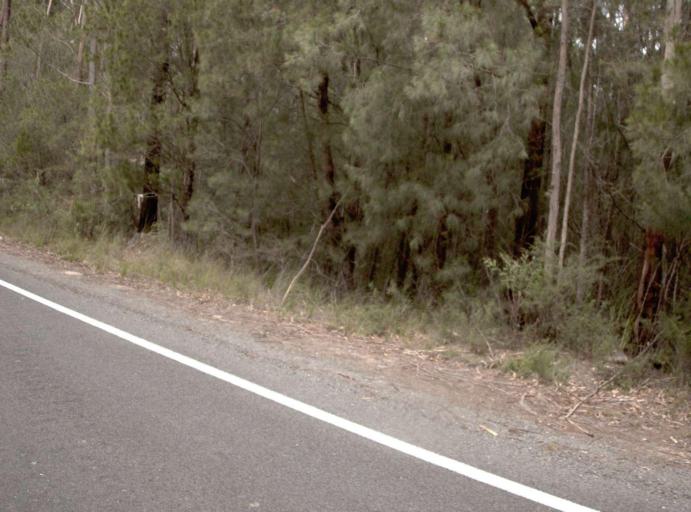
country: AU
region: New South Wales
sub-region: Bega Valley
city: Eden
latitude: -37.4975
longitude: 149.5460
